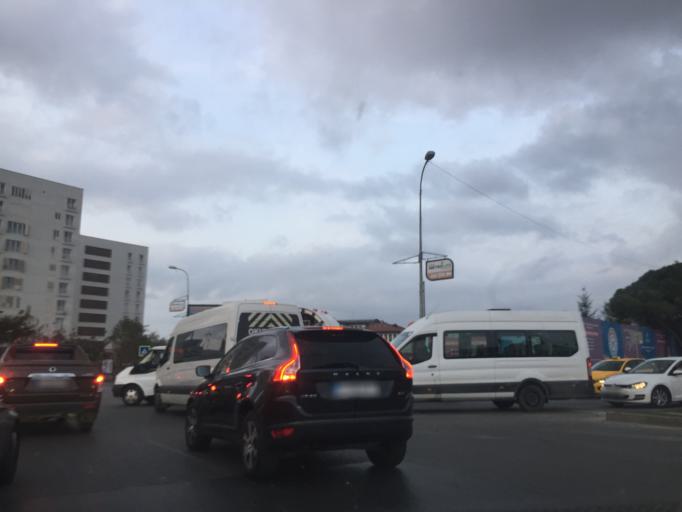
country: TR
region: Istanbul
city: Samandira
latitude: 40.9906
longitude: 29.2292
